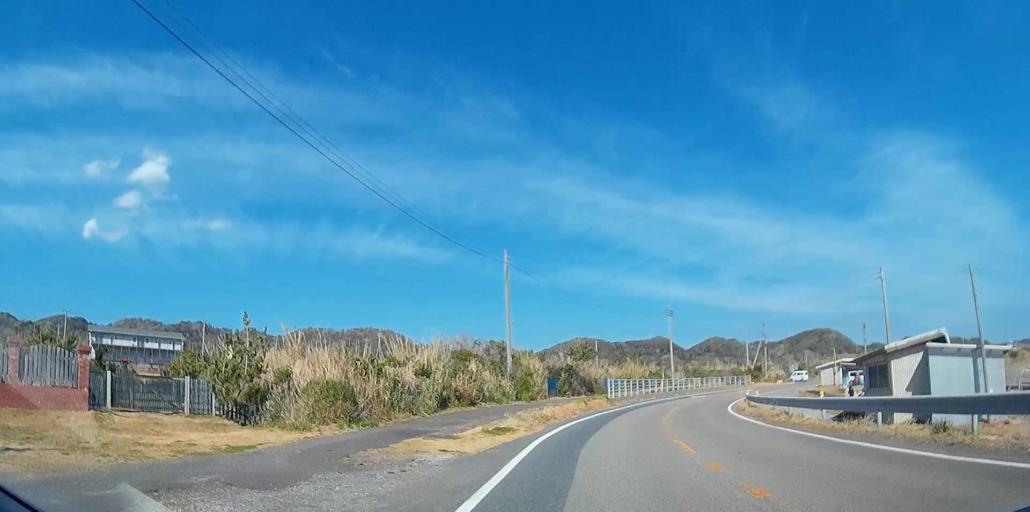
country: JP
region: Chiba
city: Tateyama
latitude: 34.9039
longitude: 139.8465
